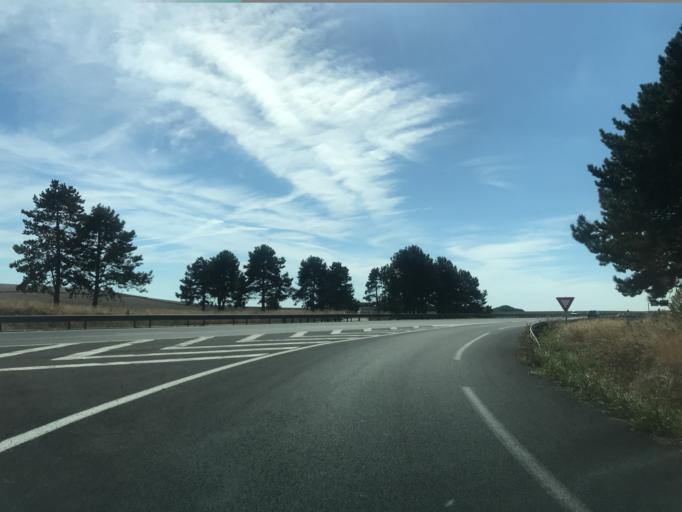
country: FR
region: Champagne-Ardenne
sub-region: Departement de la Marne
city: Chatillon-sur-Marne
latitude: 49.1578
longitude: 3.7202
